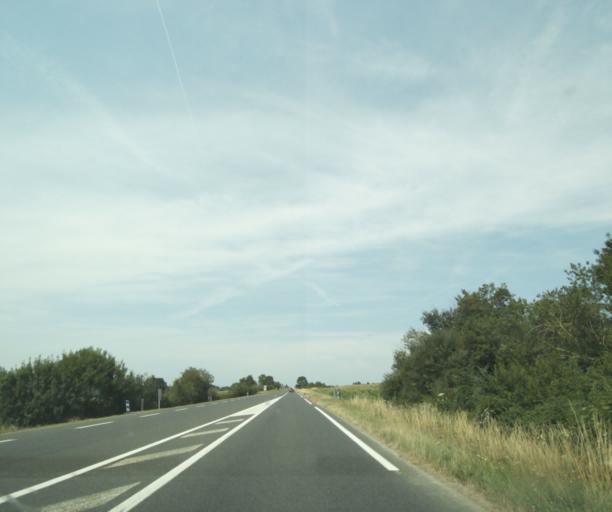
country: FR
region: Centre
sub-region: Departement d'Indre-et-Loire
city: Sorigny
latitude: 47.1858
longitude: 0.6624
